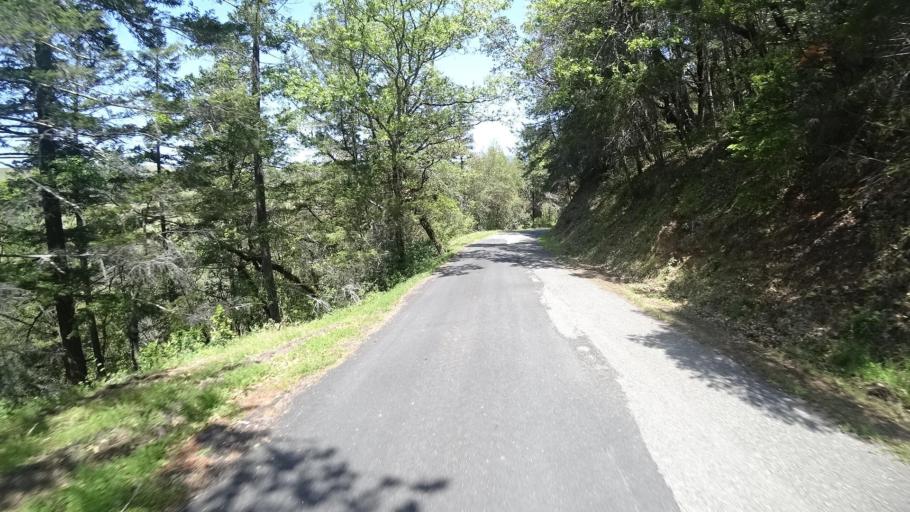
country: US
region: California
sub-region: Humboldt County
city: Redway
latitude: 40.2309
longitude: -123.6480
